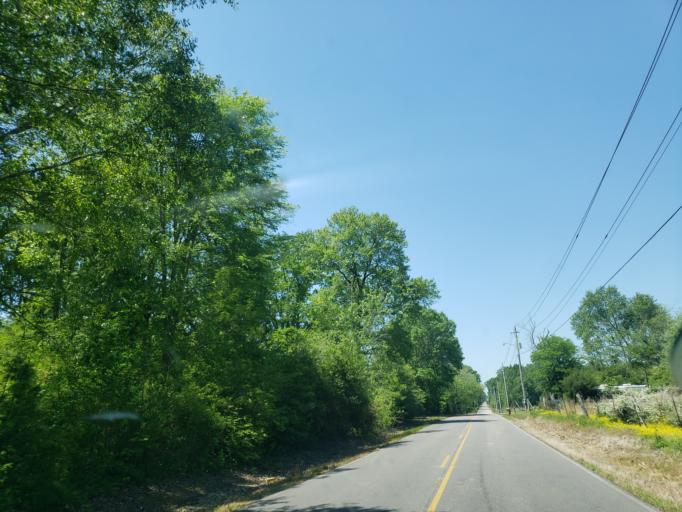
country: US
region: Alabama
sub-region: Madison County
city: Hazel Green
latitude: 34.9622
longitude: -86.6598
